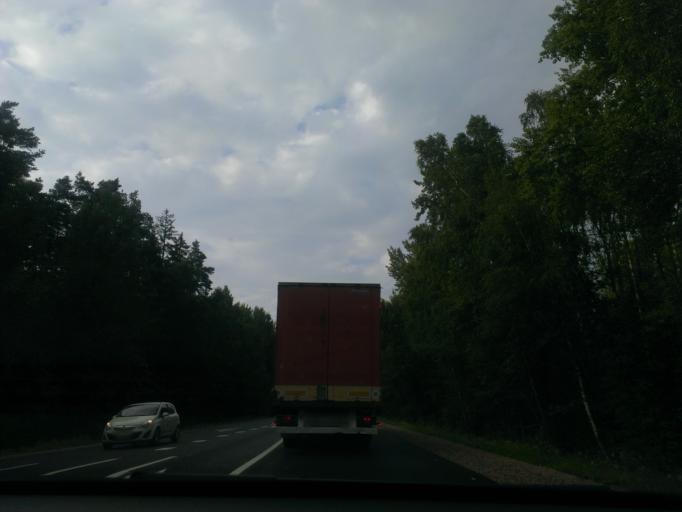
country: LV
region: Lecava
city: Iecava
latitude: 56.6627
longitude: 24.2329
